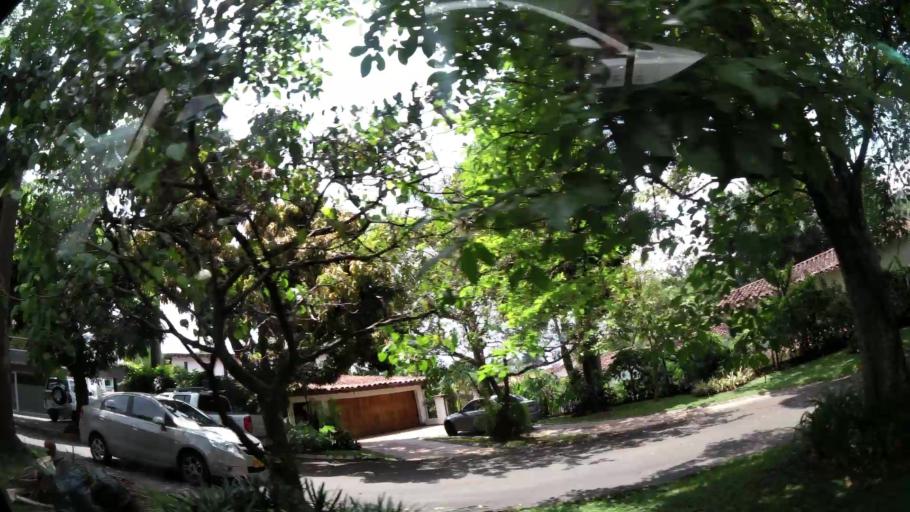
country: CO
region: Antioquia
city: Envigado
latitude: 6.1879
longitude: -75.5754
